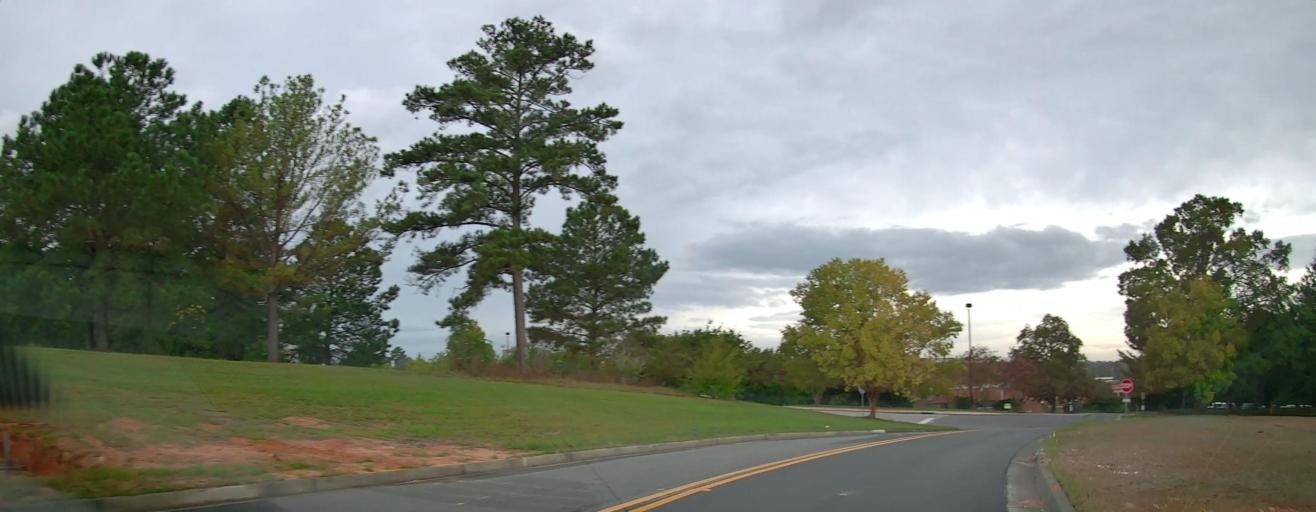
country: US
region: Georgia
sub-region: Bibb County
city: West Point
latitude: 32.8087
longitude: -83.7303
